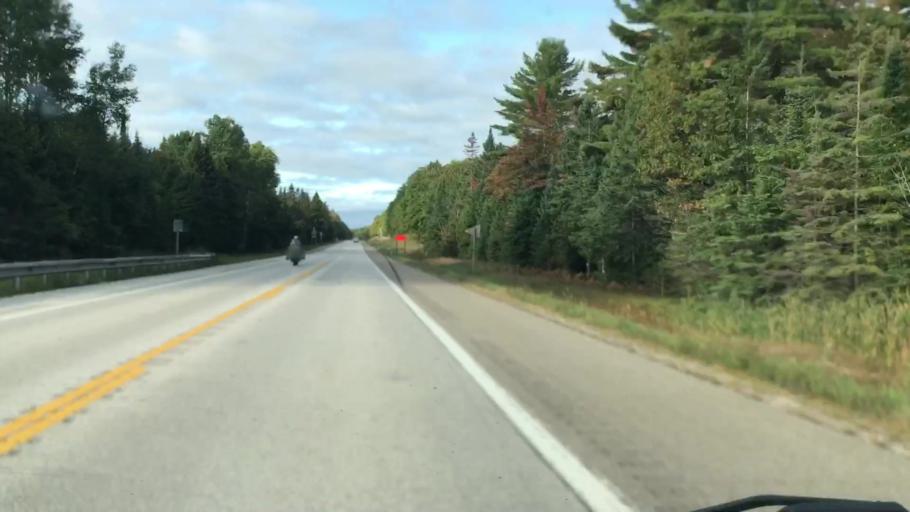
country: US
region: Michigan
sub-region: Luce County
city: Newberry
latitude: 46.3432
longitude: -85.0359
